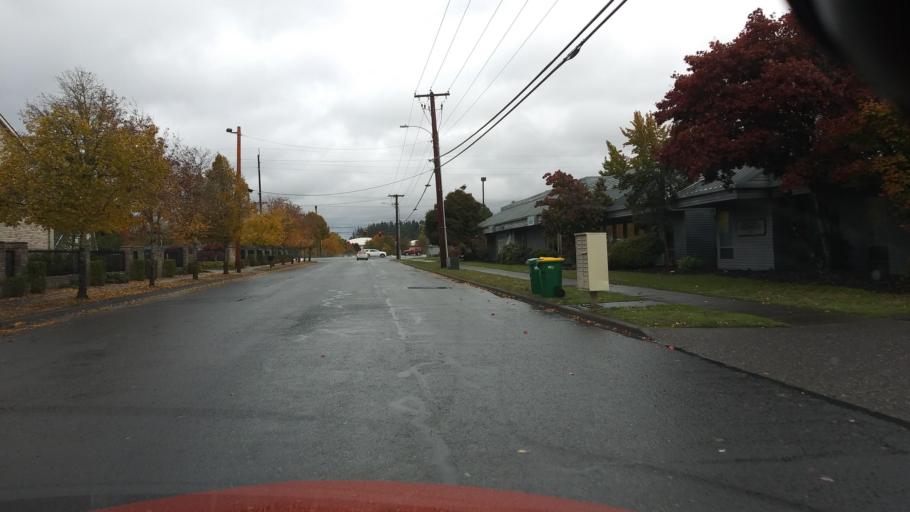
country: US
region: Oregon
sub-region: Washington County
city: Cornelius
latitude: 45.5188
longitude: -123.0758
